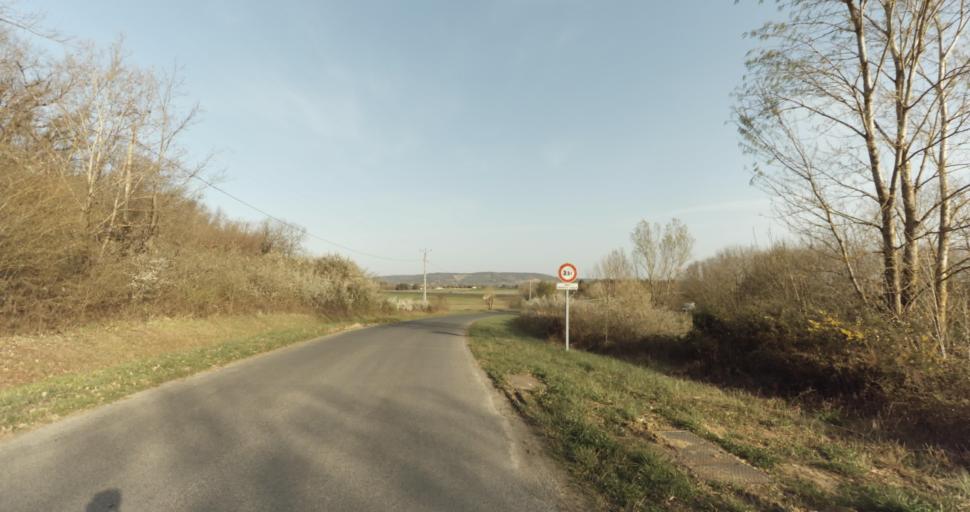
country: FR
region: Midi-Pyrenees
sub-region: Departement du Tarn
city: Saint-Sulpice-la-Pointe
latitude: 43.7506
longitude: 1.6867
